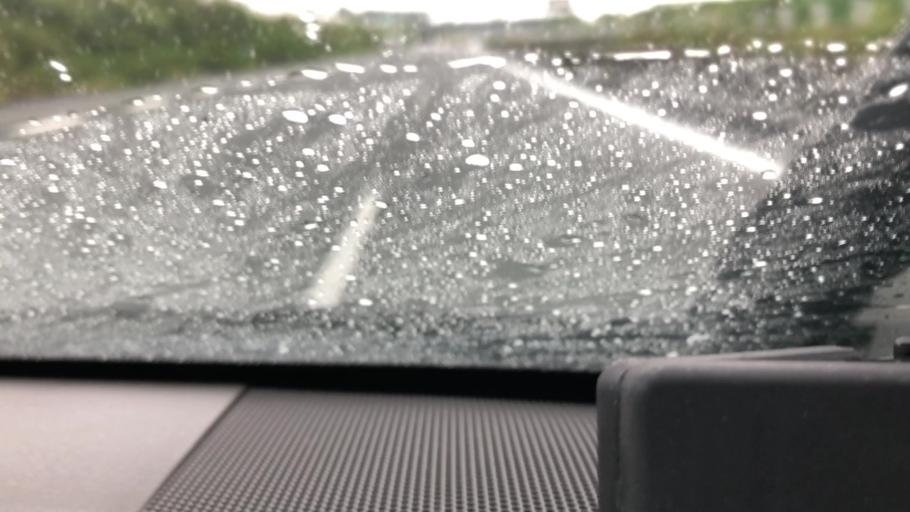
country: JP
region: Shizuoka
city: Fuji
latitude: 35.2026
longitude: 138.6699
